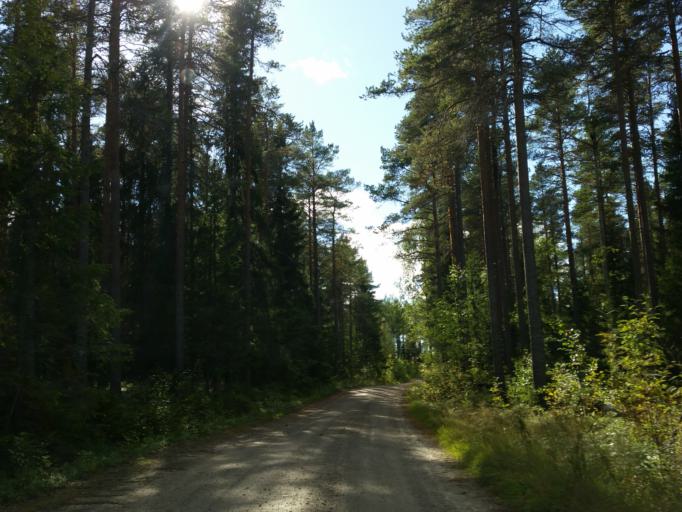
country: SE
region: Vaesterbotten
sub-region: Robertsfors Kommun
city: Robertsfors
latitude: 64.0468
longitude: 20.8703
